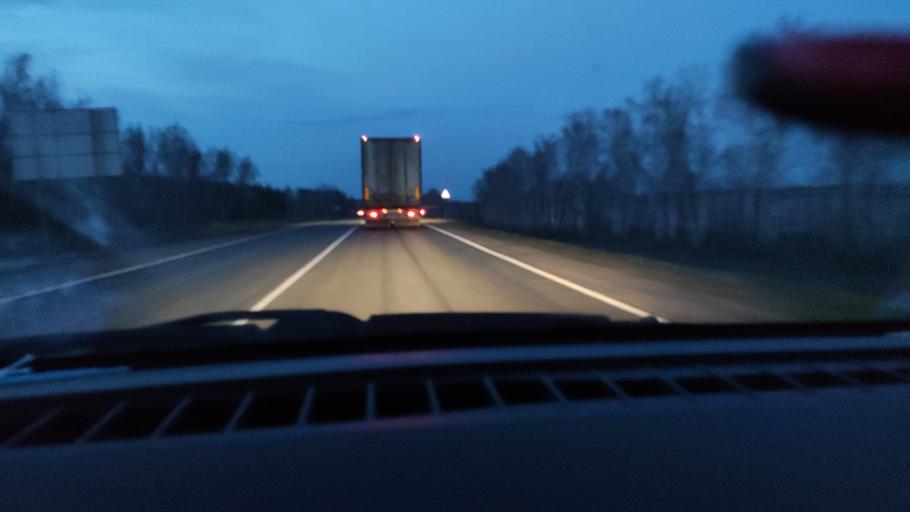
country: RU
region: Saratov
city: Sennoy
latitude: 52.1211
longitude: 46.8459
